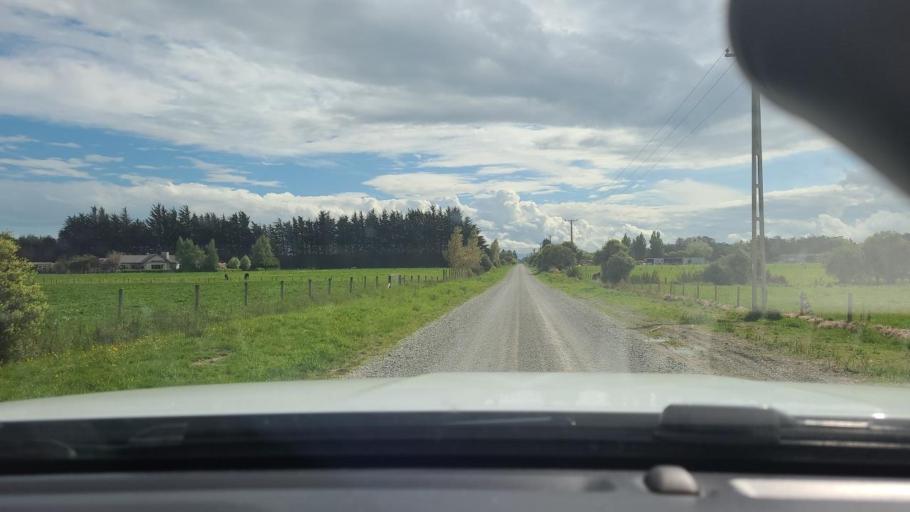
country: NZ
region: Southland
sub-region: Southland District
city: Winton
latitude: -46.1251
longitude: 168.3494
